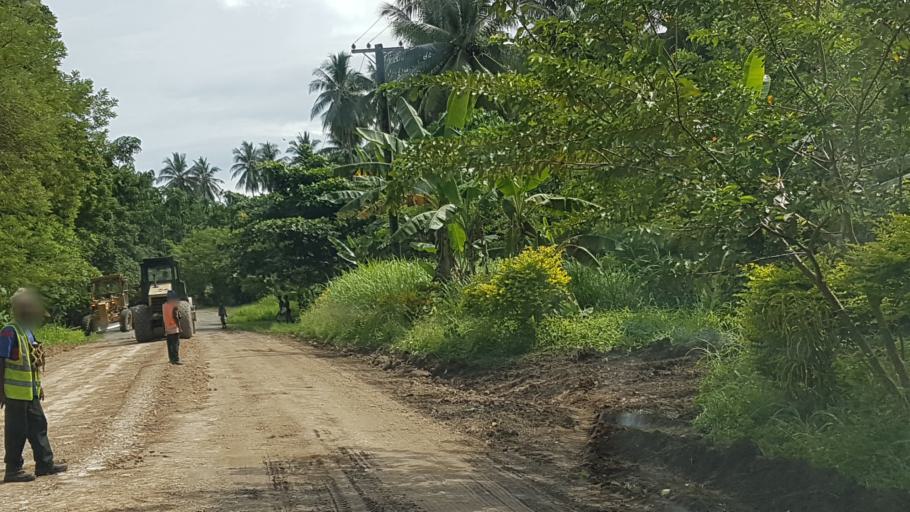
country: PG
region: Madang
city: Madang
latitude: -4.8722
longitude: 145.8020
